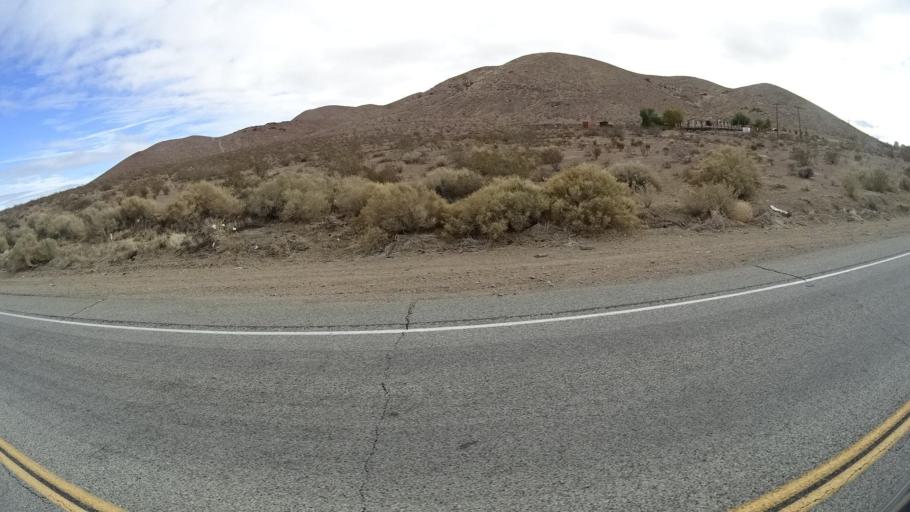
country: US
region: California
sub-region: Kern County
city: Rosamond
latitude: 34.8846
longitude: -118.2917
